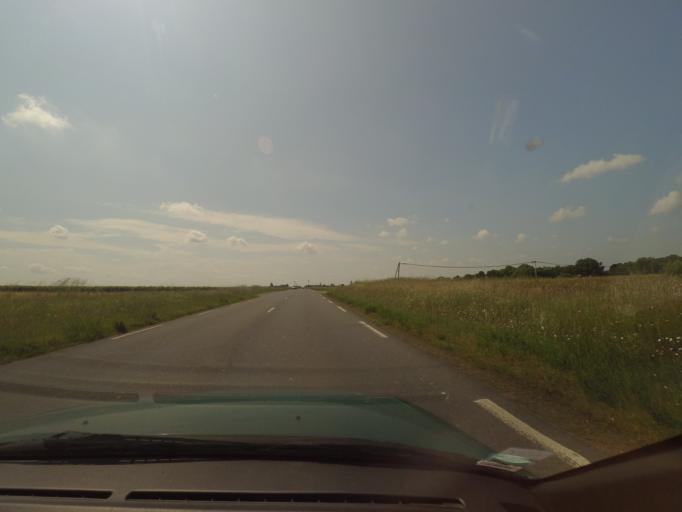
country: FR
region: Pays de la Loire
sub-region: Departement de la Loire-Atlantique
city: Mouzillon
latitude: 47.1318
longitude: -1.2825
